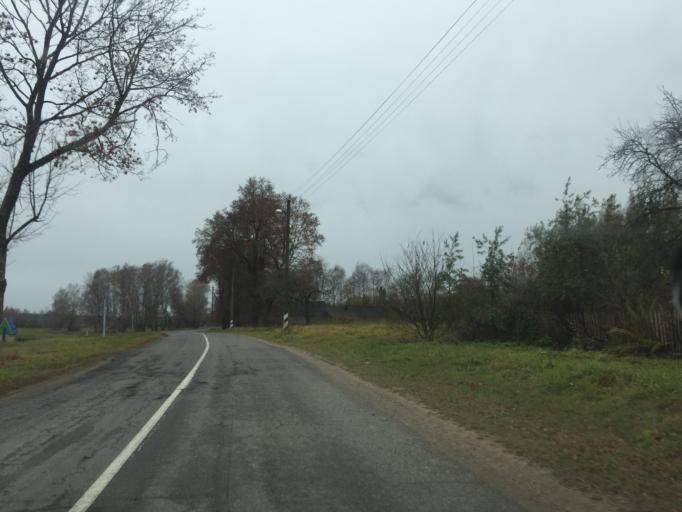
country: BY
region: Mogilev
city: Chavusy
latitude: 53.8825
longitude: 31.0538
